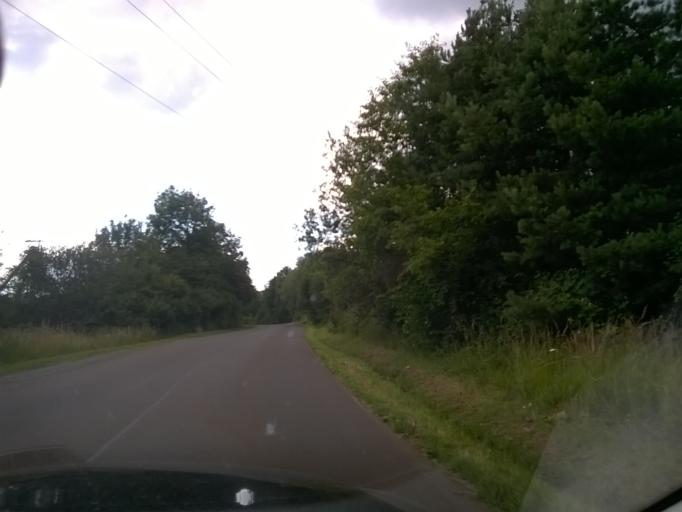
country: SK
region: Banskobystricky
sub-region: Okres Banska Bystrica
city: Banska Stiavnica
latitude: 48.4683
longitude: 18.8962
